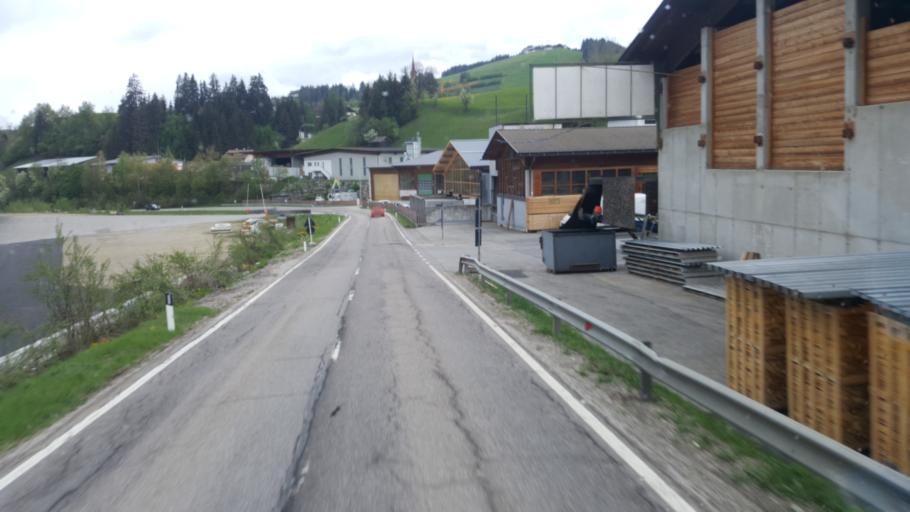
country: IT
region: Trentino-Alto Adige
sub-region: Bolzano
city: Monguelfo
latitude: 46.7666
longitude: 12.1227
